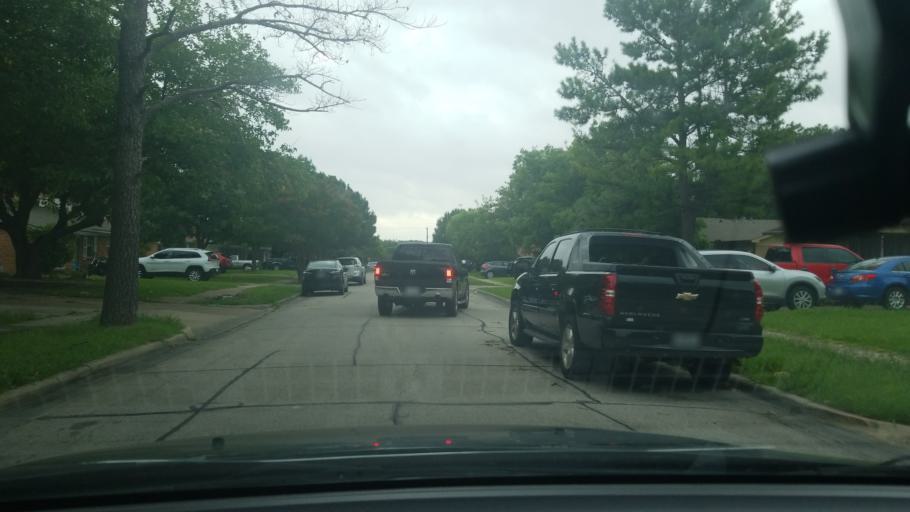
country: US
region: Texas
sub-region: Dallas County
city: Mesquite
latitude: 32.7908
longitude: -96.6316
